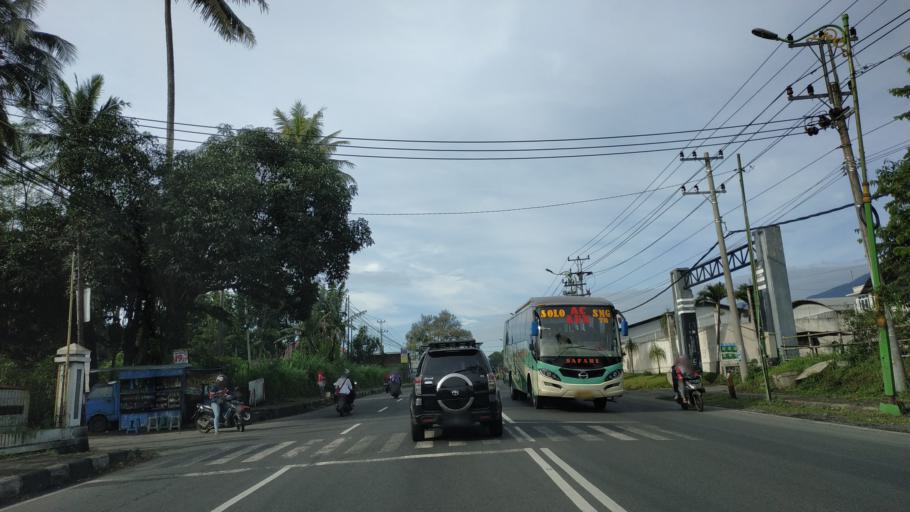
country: ID
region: Central Java
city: Salatiga
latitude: -7.3734
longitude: 110.5151
